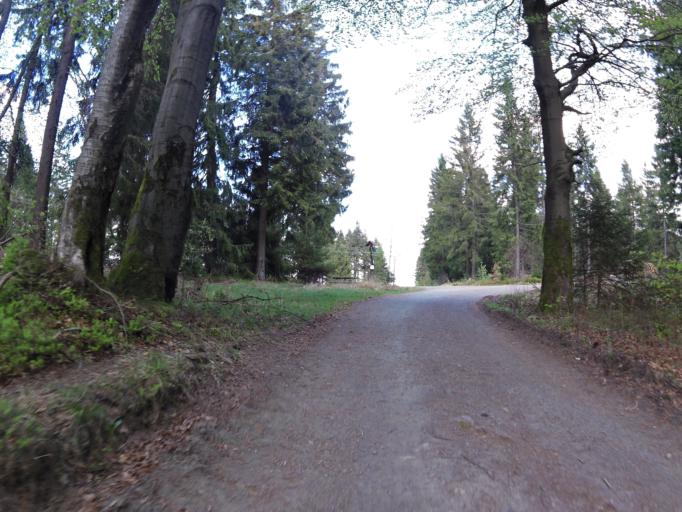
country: DE
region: Thuringia
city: Finsterbergen
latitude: 50.7845
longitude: 10.5438
